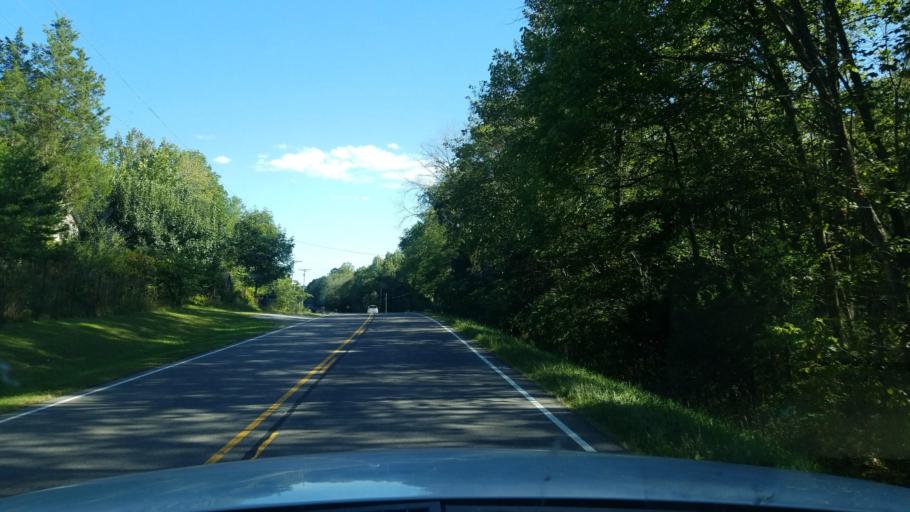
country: US
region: Illinois
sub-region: Saline County
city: Harrisburg
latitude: 37.6074
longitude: -88.4627
